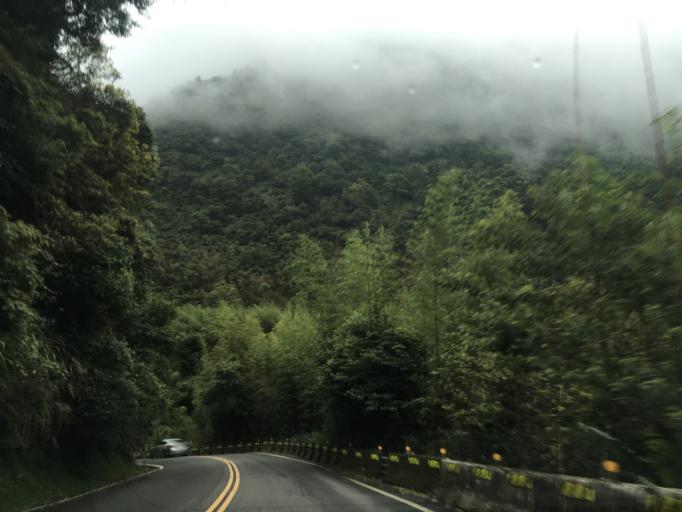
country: TW
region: Taiwan
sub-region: Chiayi
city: Jiayi Shi
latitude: 23.4979
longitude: 120.7016
